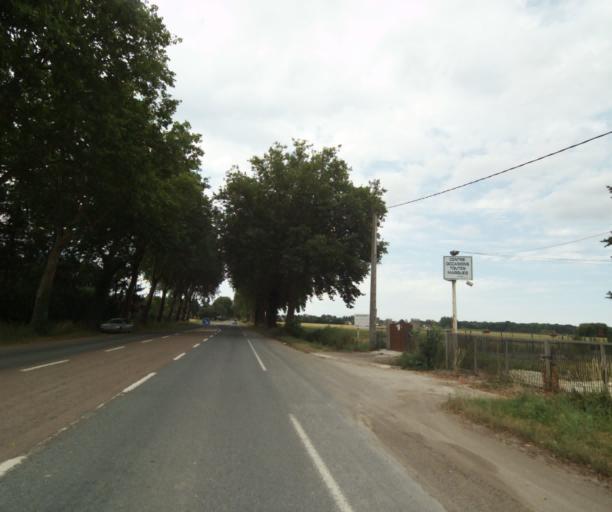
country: FR
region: Ile-de-France
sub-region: Departement de Seine-et-Marne
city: Chailly-en-Biere
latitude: 48.4561
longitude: 2.6169
